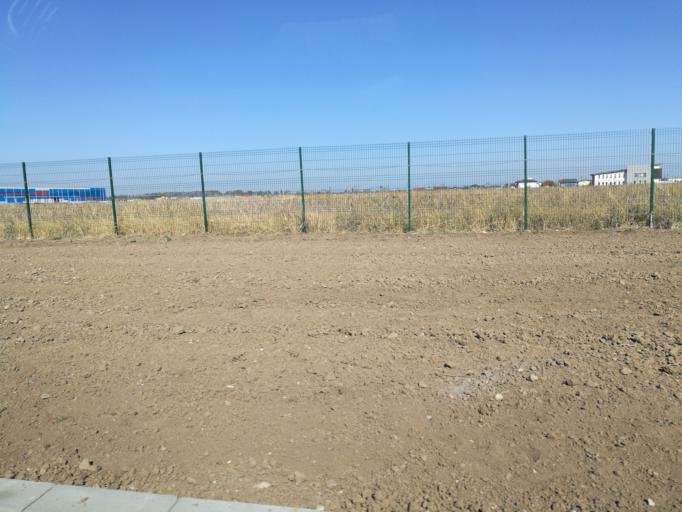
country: RO
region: Giurgiu
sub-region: Comuna Joita
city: Bacu
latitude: 44.4643
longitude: 25.8798
